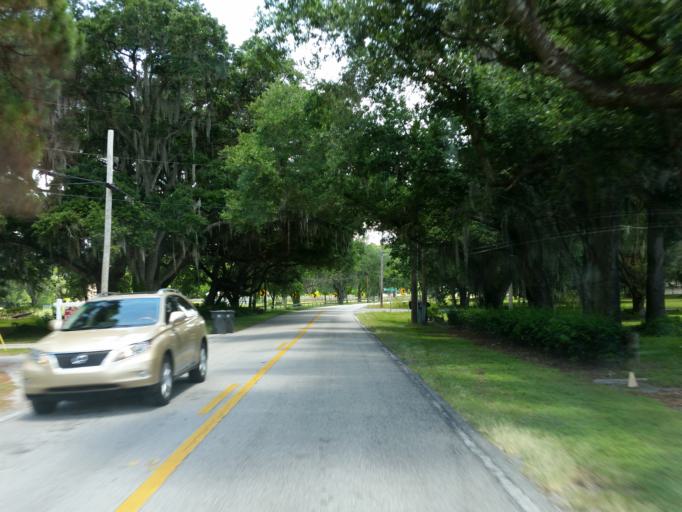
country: US
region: Florida
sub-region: Hillsborough County
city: Dover
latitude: 28.0398
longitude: -82.1778
